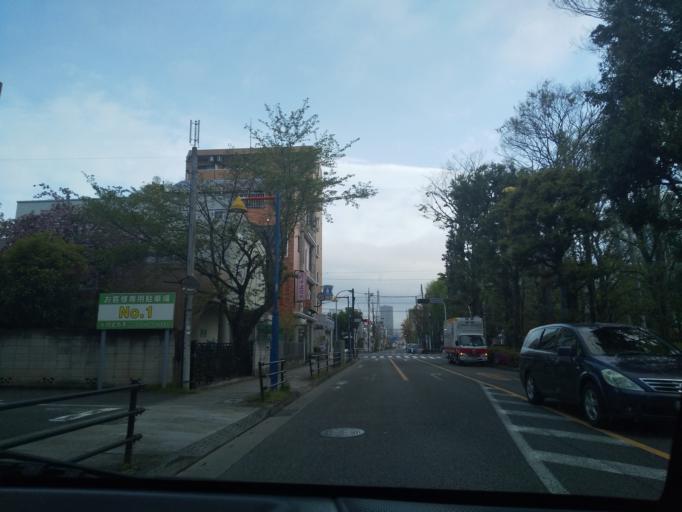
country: JP
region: Tokyo
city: Kokubunji
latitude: 35.6853
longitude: 139.4796
